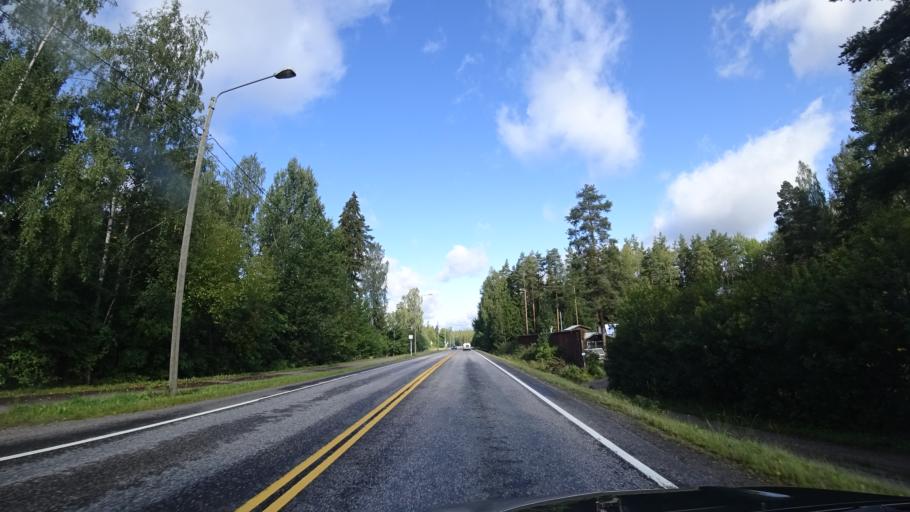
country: FI
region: Uusimaa
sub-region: Helsinki
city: Tuusula
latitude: 60.4403
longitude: 24.9780
